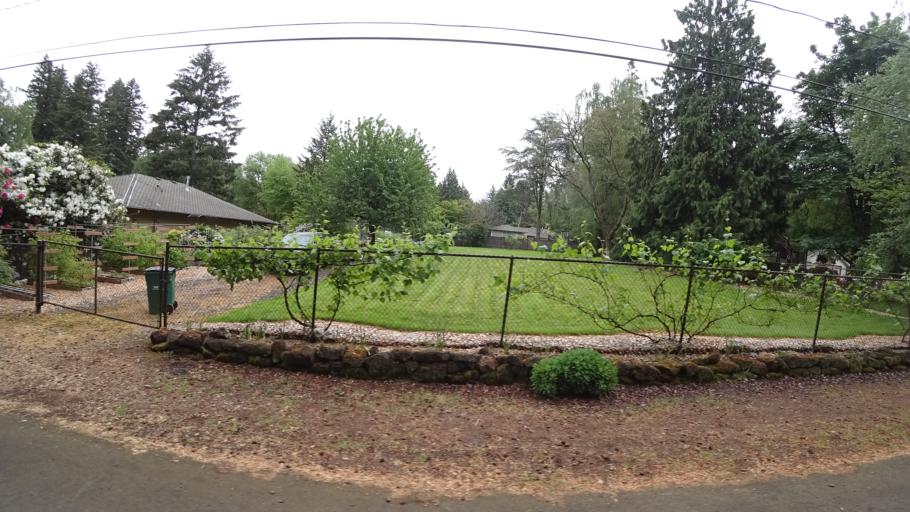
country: US
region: Oregon
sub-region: Washington County
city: Garden Home-Whitford
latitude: 45.4690
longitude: -122.7624
